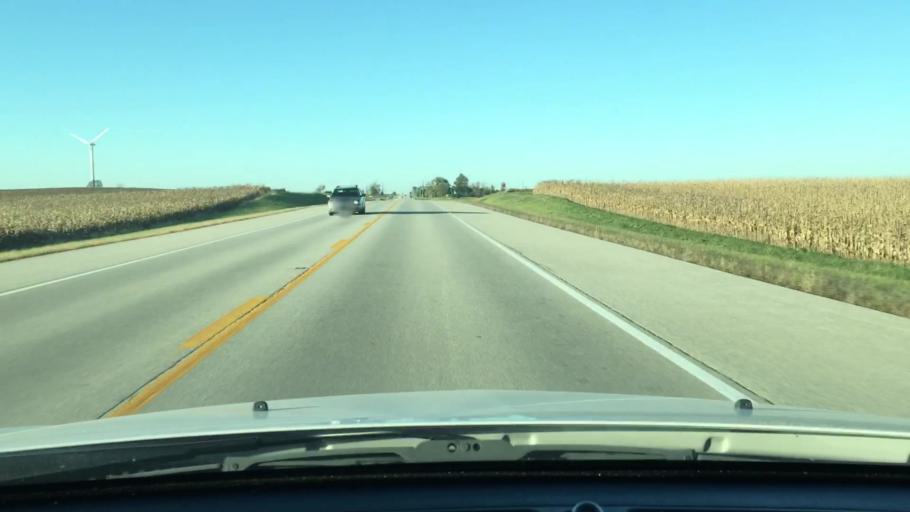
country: US
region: Illinois
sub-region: DeKalb County
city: Waterman
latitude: 41.8116
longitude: -88.7539
